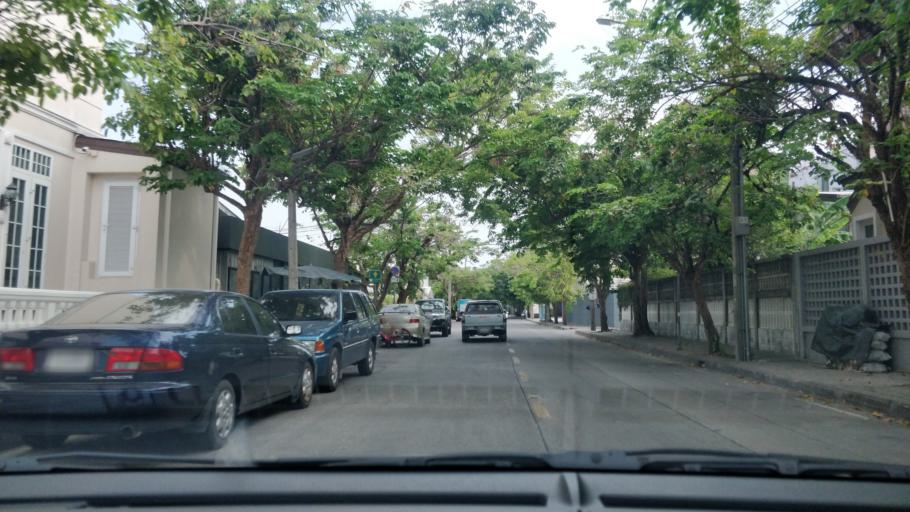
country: TH
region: Bangkok
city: Suan Luang
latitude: 13.7449
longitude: 100.6318
